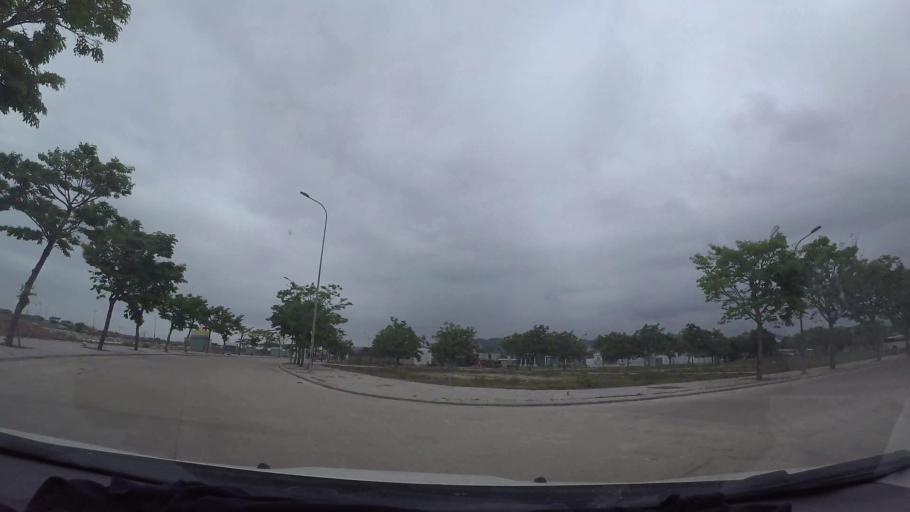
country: VN
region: Da Nang
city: Lien Chieu
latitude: 16.1058
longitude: 108.1206
